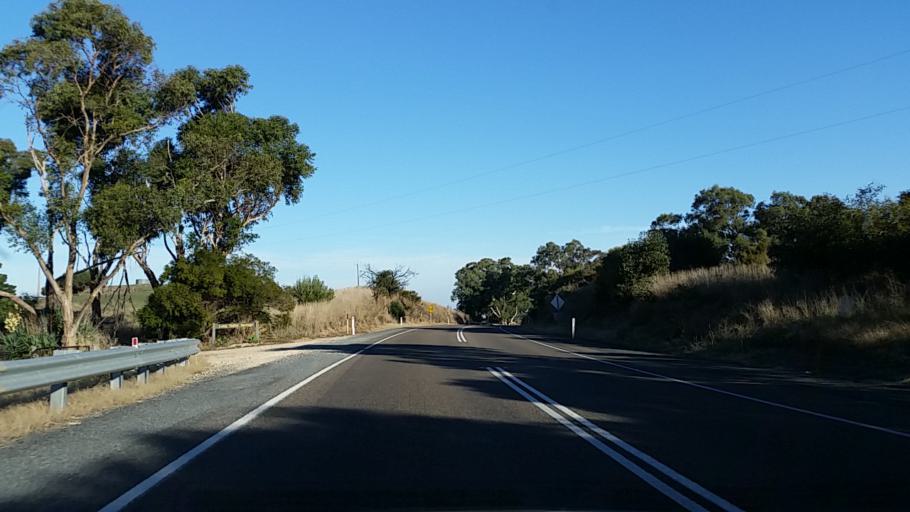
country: AU
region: South Australia
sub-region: Mount Barker
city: Macclesfield
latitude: -35.1888
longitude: 138.8939
